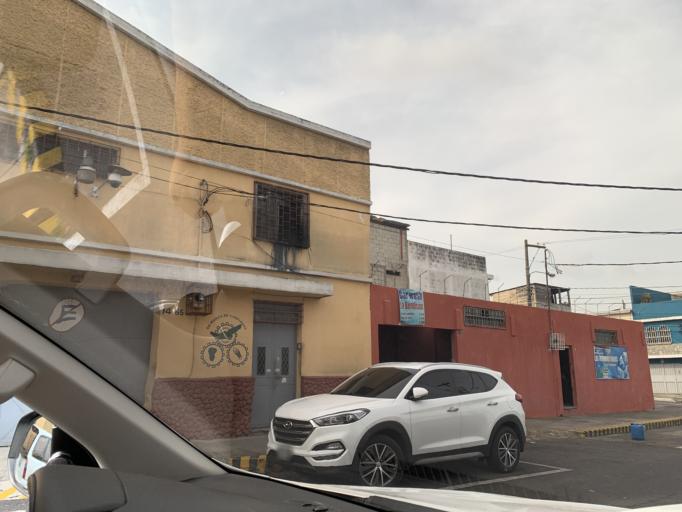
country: GT
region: Guatemala
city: Guatemala City
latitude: 14.6015
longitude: -90.5418
